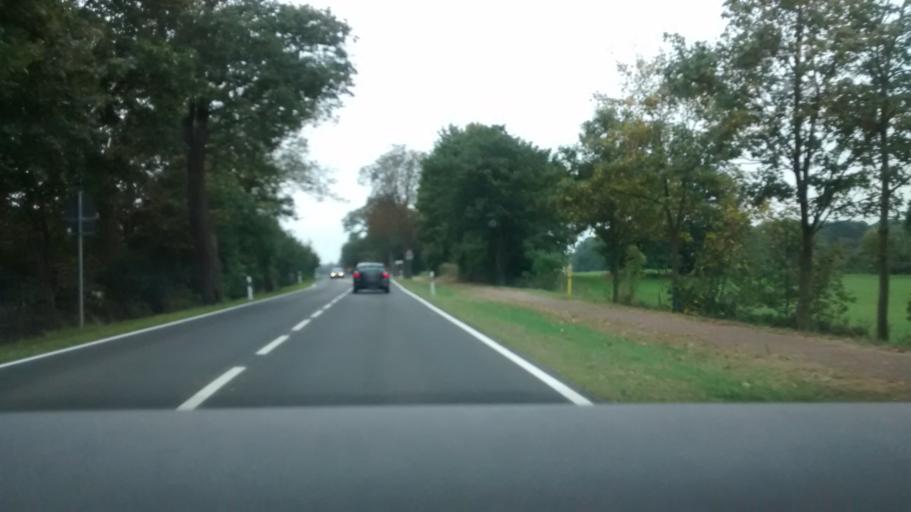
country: DE
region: Mecklenburg-Vorpommern
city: Mecklenburg
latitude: 53.8145
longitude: 11.4443
